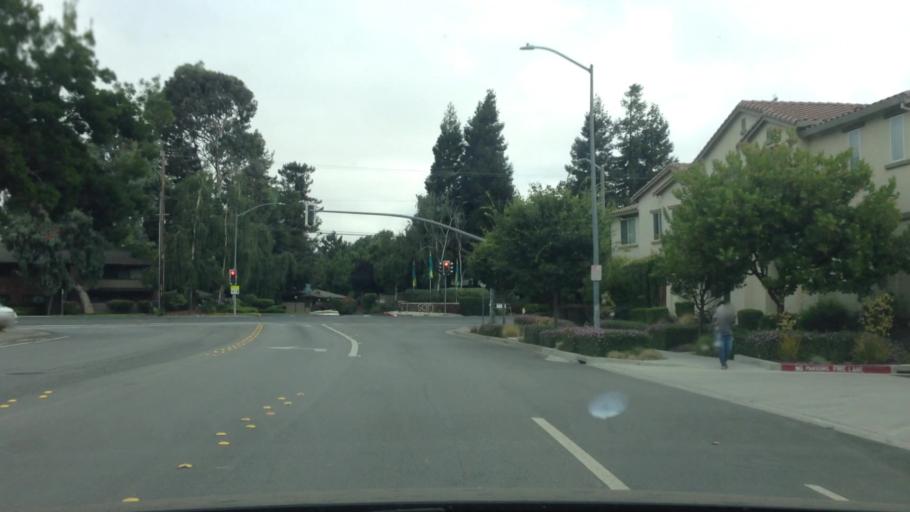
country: US
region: California
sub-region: Alameda County
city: Fremont
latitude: 37.5653
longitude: -121.9753
